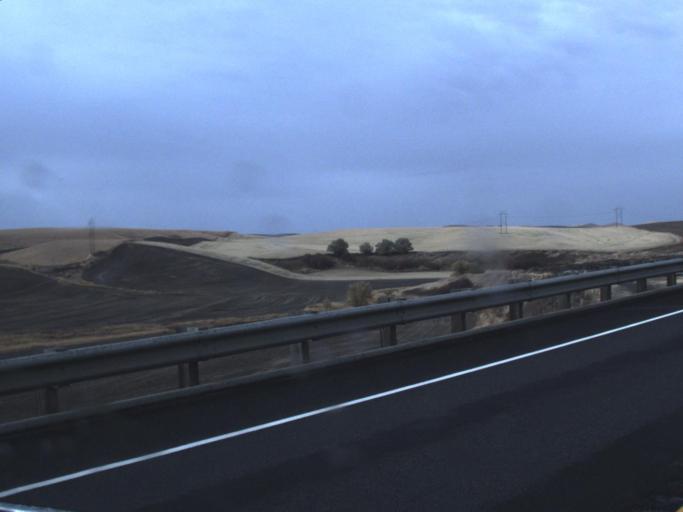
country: US
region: Washington
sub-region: Whitman County
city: Pullman
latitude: 46.5896
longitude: -117.1693
